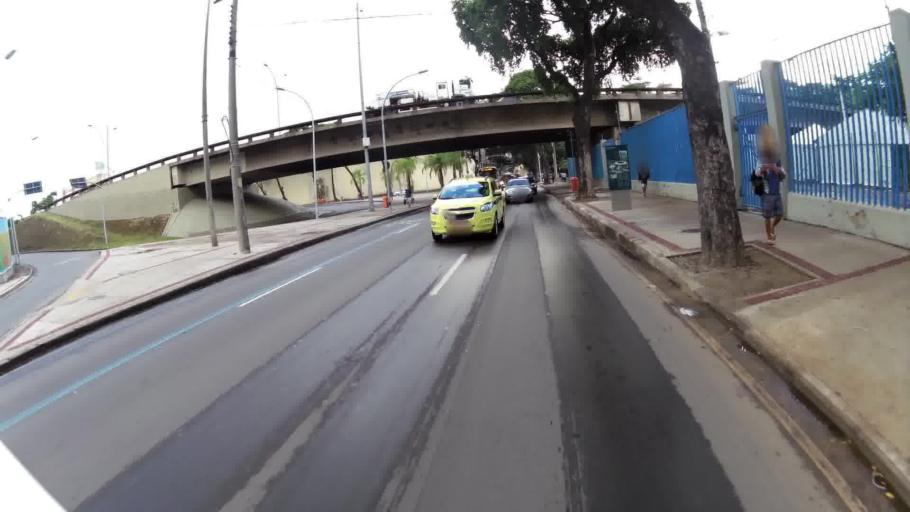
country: BR
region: Rio de Janeiro
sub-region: Rio De Janeiro
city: Rio de Janeiro
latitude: -22.9119
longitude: -43.1962
